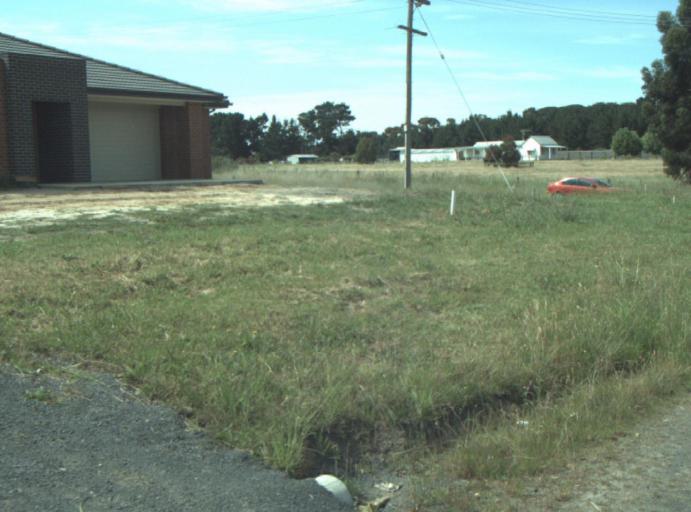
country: AU
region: Victoria
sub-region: Greater Geelong
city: Clifton Springs
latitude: -38.1817
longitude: 144.5691
